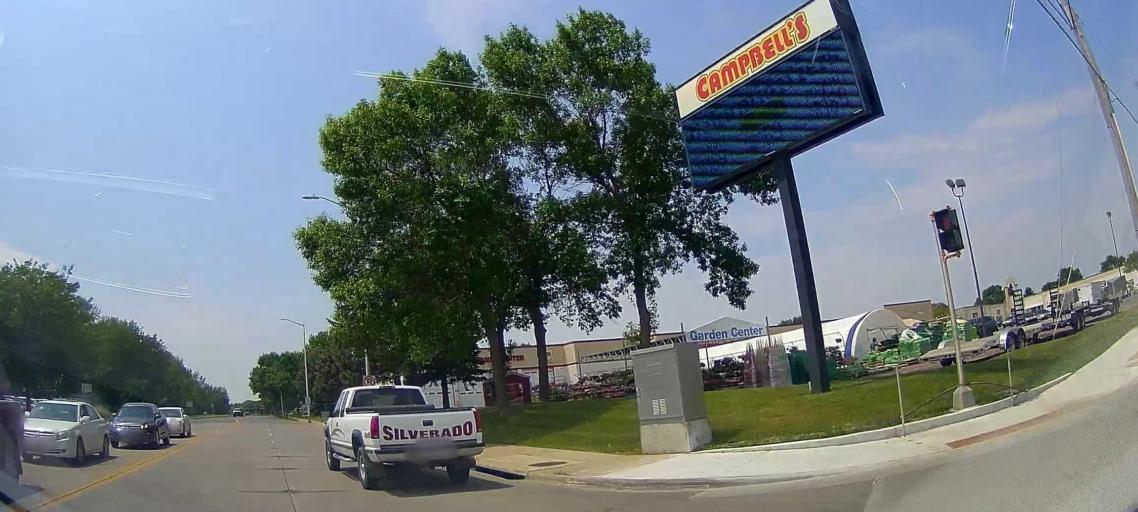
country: US
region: South Dakota
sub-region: Minnehaha County
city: Sioux Falls
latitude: 43.5085
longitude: -96.7512
